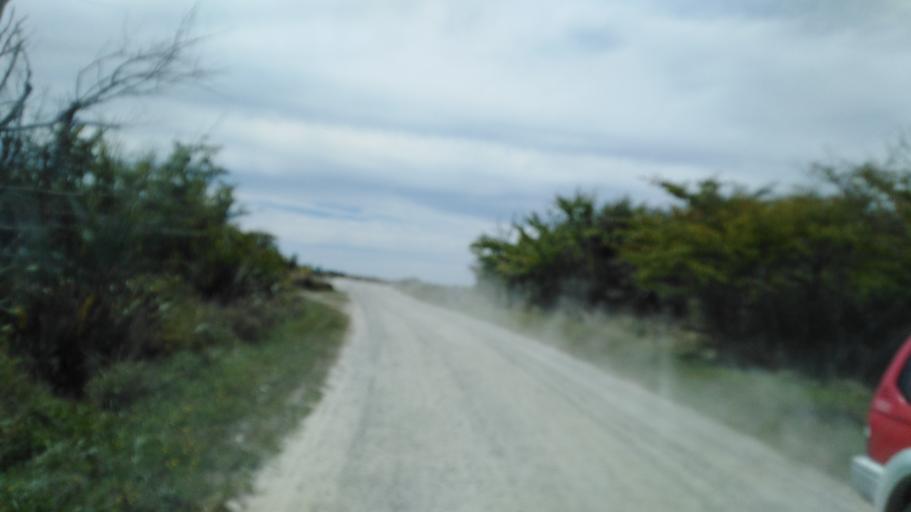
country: NZ
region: West Coast
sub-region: Buller District
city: Westport
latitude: -41.7357
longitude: 171.6055
